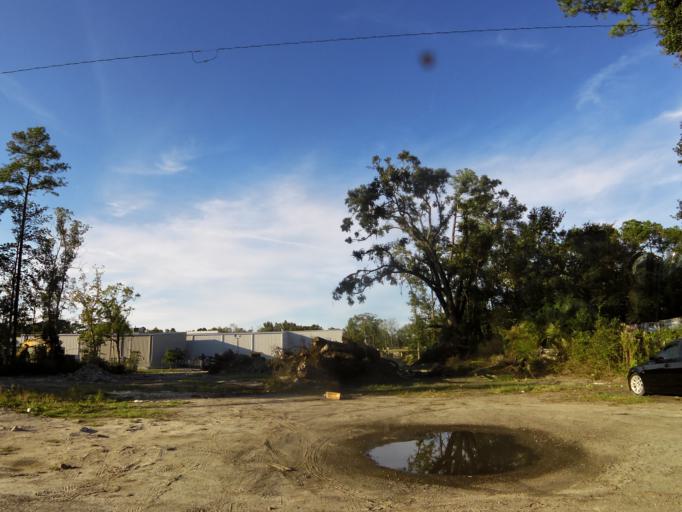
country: US
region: Florida
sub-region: Duval County
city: Jacksonville
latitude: 30.3662
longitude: -81.7314
